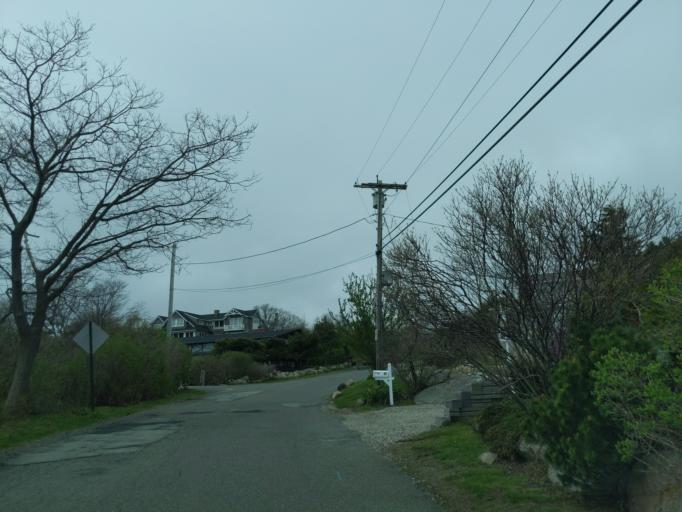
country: US
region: Massachusetts
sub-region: Essex County
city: Rockport
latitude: 42.6414
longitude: -70.5966
